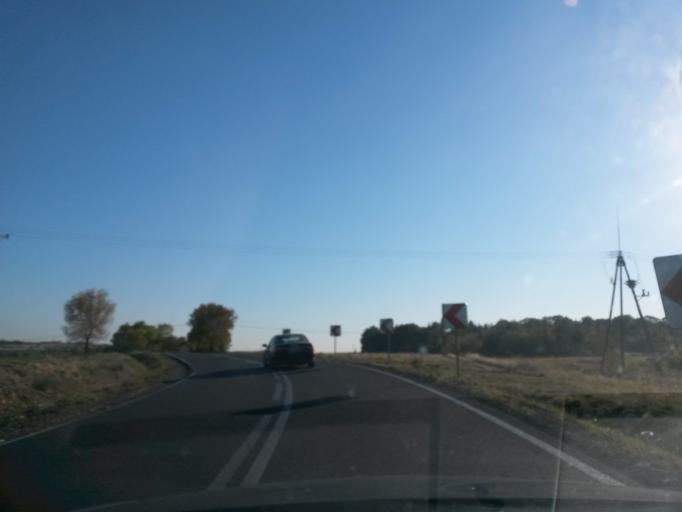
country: PL
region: Lower Silesian Voivodeship
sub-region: Powiat swidnicki
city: Strzegom
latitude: 50.9992
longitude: 16.3838
